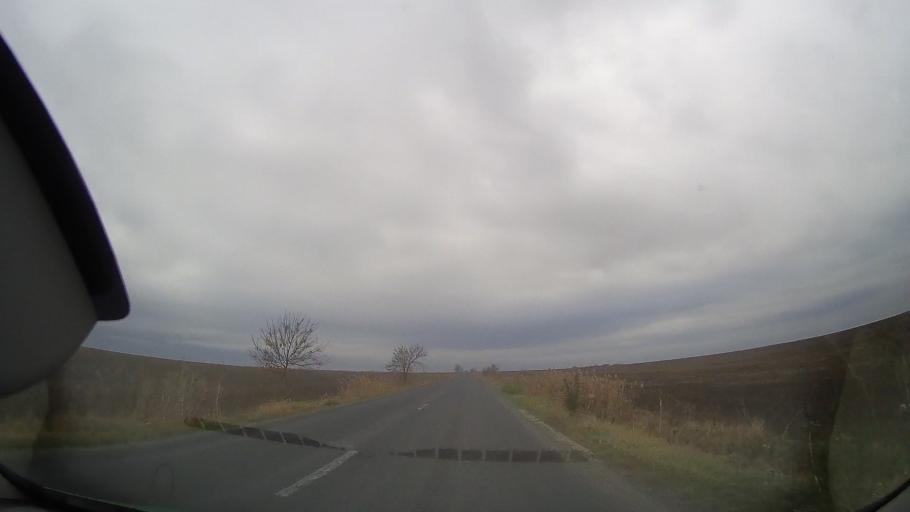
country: RO
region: Buzau
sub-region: Comuna Padina
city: Padina
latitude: 44.8021
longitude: 27.1341
